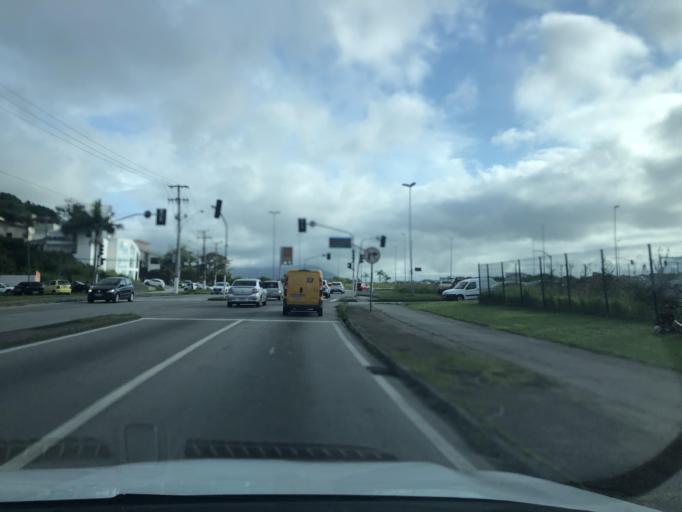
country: BR
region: Santa Catarina
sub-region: Florianopolis
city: Saco dos Limoes
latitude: -27.6151
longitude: -48.5273
